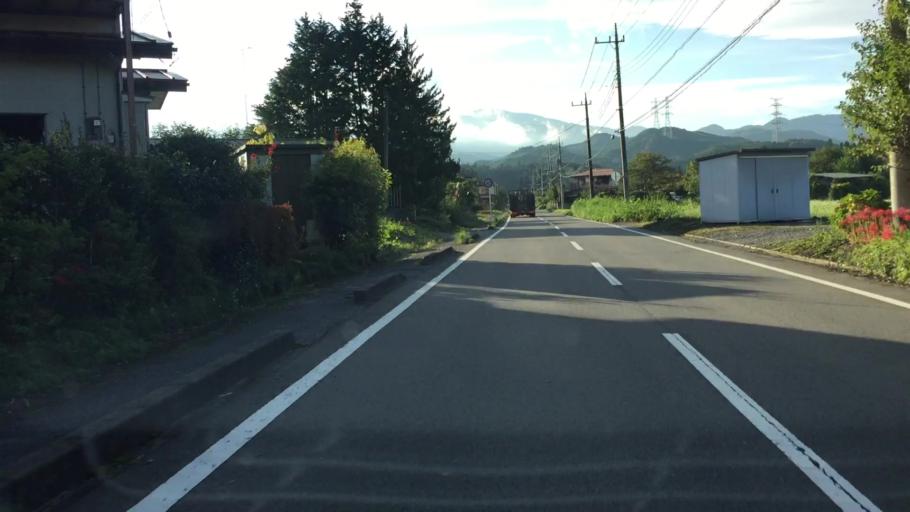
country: JP
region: Tochigi
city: Imaichi
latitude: 36.7609
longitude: 139.7040
